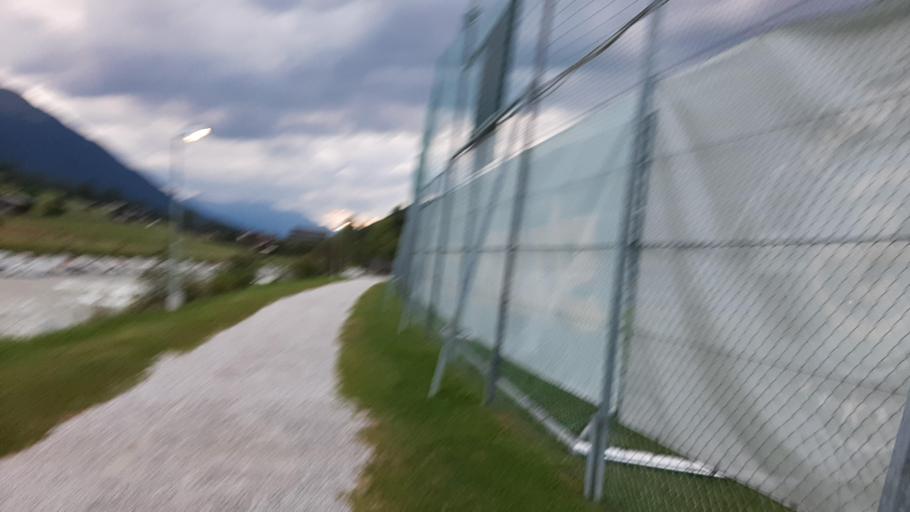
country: AT
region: Tyrol
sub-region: Politischer Bezirk Innsbruck Land
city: Neustift im Stubaital
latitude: 47.1242
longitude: 11.3288
